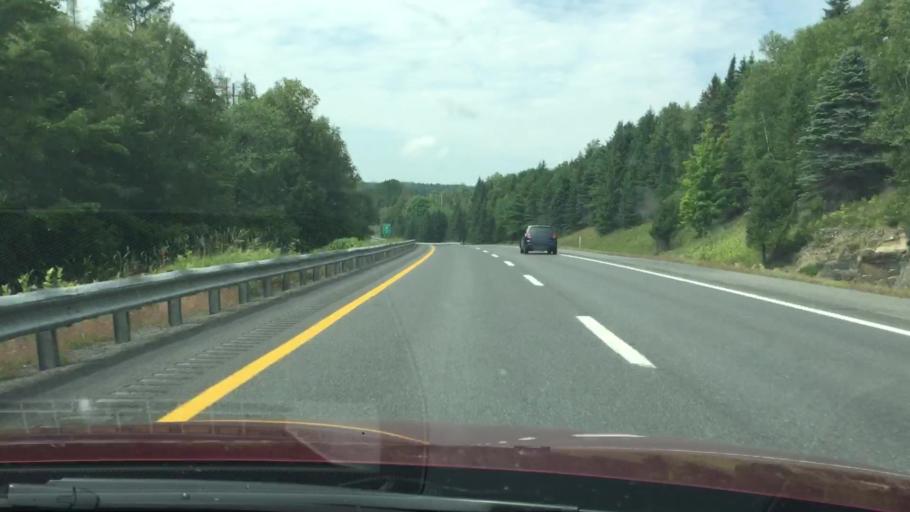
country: US
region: Maine
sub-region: Aroostook County
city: Hodgdon
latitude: 46.1451
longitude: -68.0506
